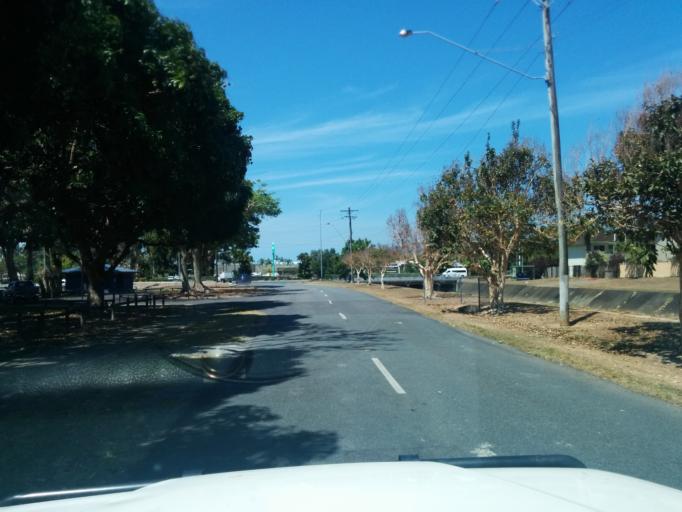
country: AU
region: Queensland
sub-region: Cairns
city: Woree
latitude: -16.9469
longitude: 145.7375
